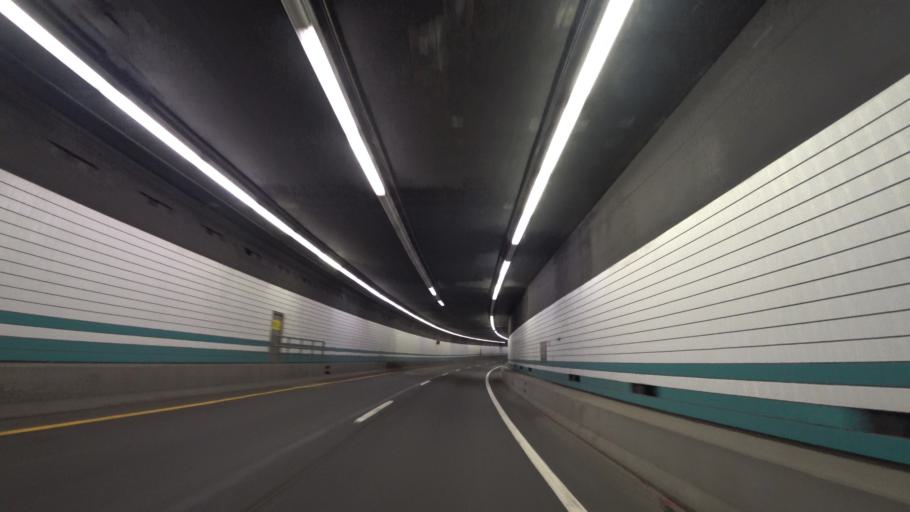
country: US
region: Massachusetts
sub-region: Suffolk County
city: Boston
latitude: 42.3444
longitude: -71.0601
